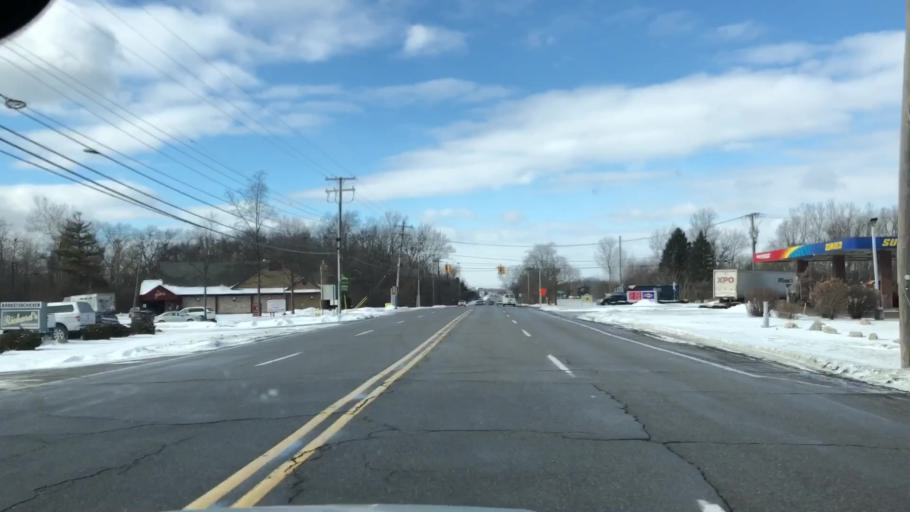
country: US
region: Michigan
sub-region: Wayne County
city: Plymouth
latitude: 42.3716
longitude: -83.4296
